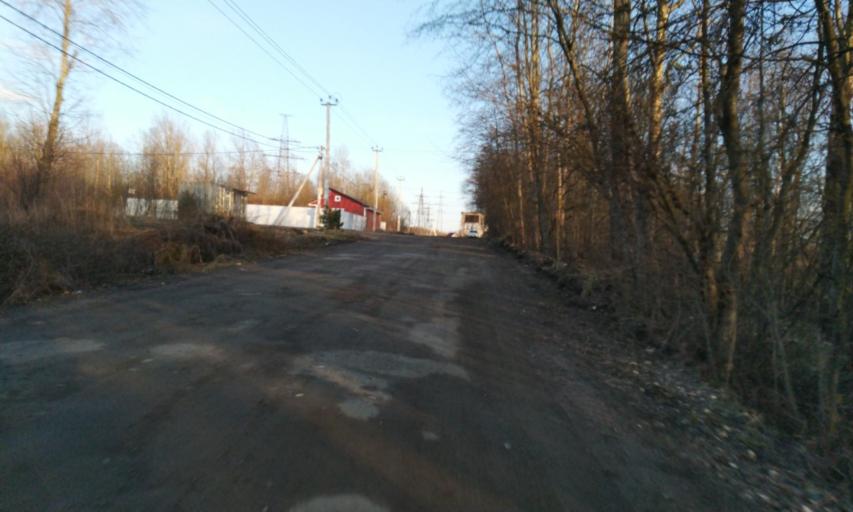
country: RU
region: Leningrad
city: Novoye Devyatkino
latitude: 60.0919
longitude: 30.4580
